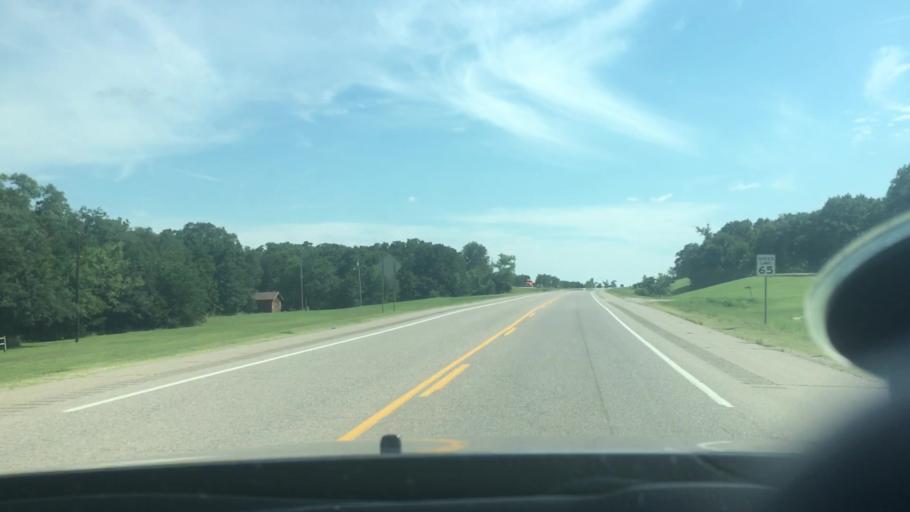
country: US
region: Oklahoma
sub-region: Seminole County
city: Seminole
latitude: 35.1444
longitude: -96.6759
